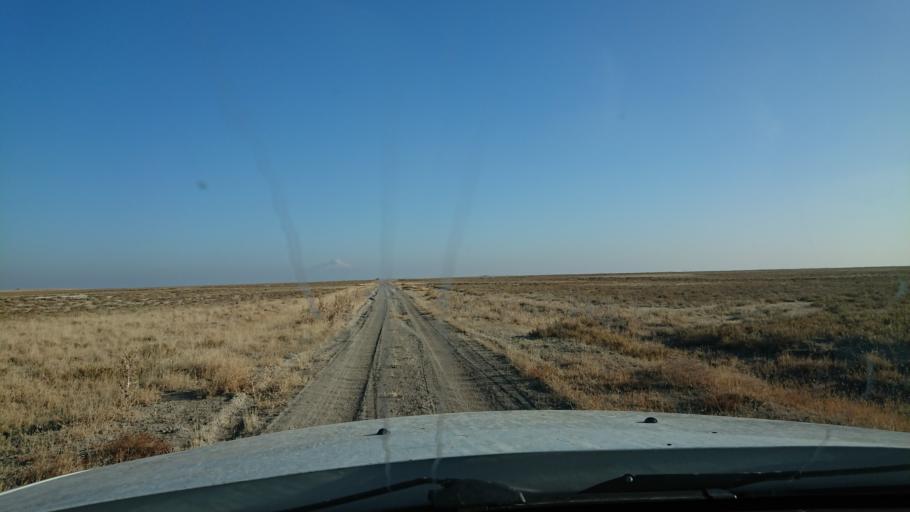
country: TR
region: Aksaray
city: Sultanhani
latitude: 38.4033
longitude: 33.5765
